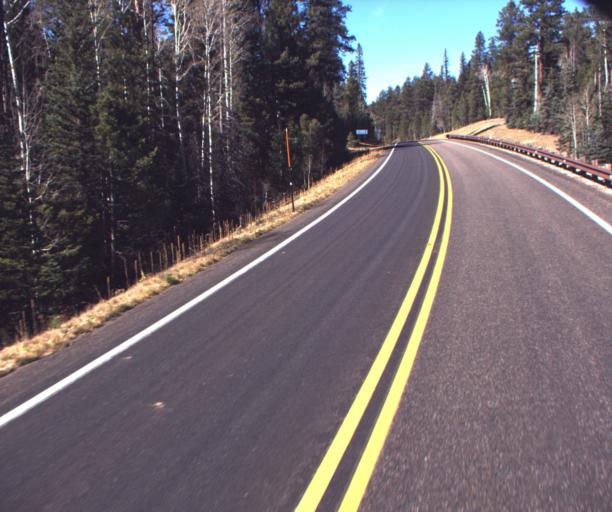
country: US
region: Arizona
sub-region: Coconino County
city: Grand Canyon
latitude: 36.5122
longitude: -112.1369
